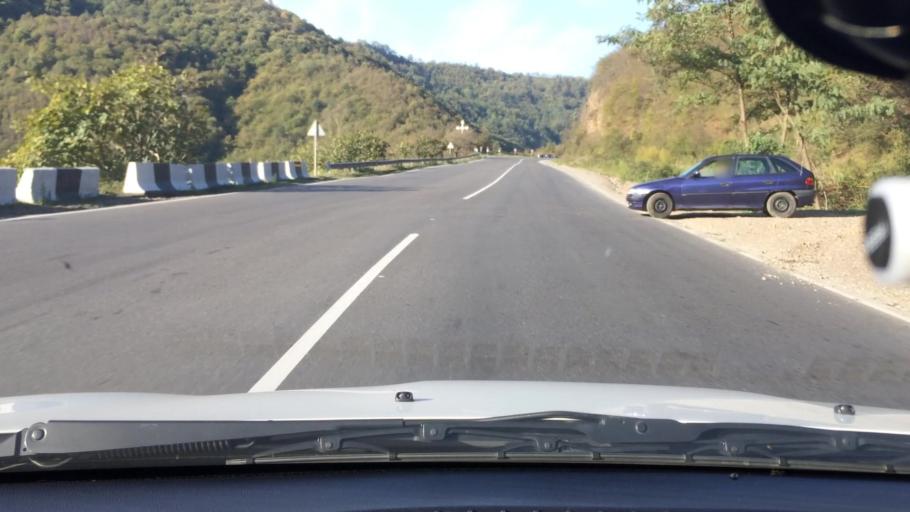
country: GE
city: Shorapani
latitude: 42.0840
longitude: 43.1552
